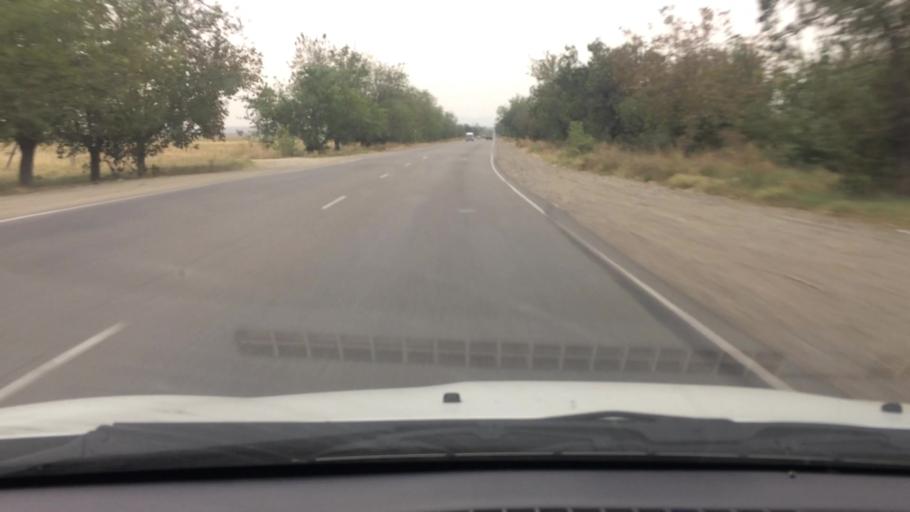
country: GE
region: Kvemo Kartli
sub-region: Marneuli
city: Marneuli
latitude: 41.5672
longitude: 44.7754
